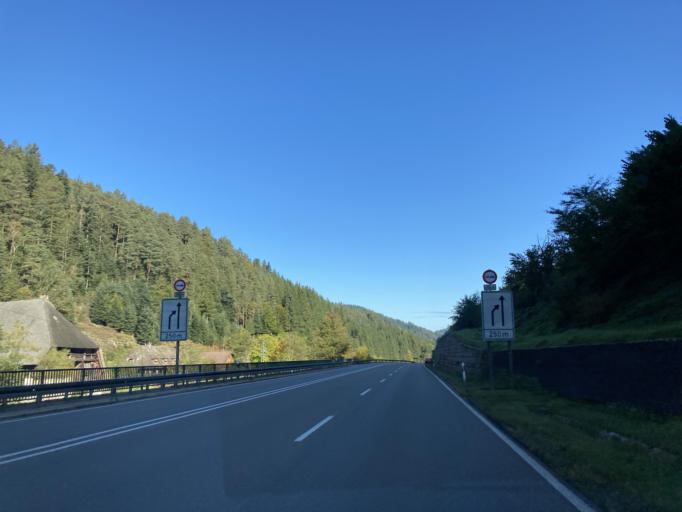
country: DE
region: Baden-Wuerttemberg
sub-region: Freiburg Region
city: Hornberg
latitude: 48.1798
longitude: 8.2307
